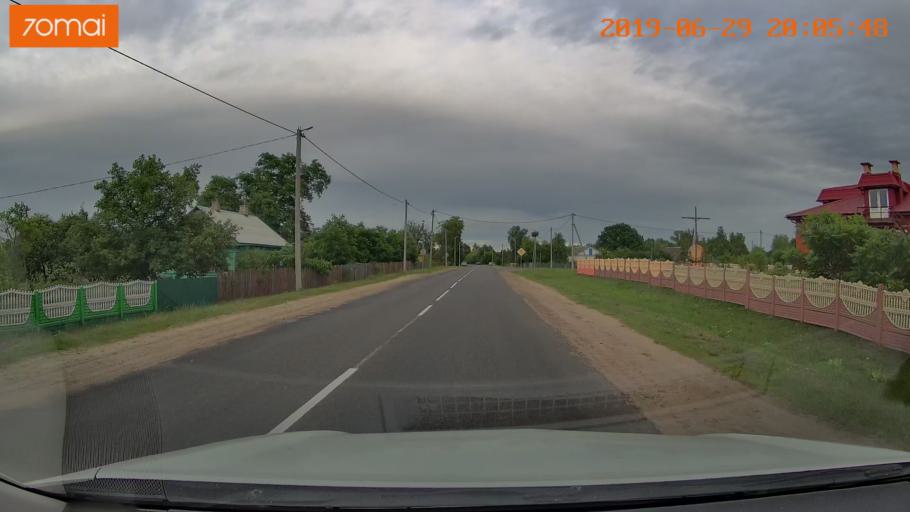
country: BY
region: Brest
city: Lahishyn
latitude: 52.3385
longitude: 26.0026
